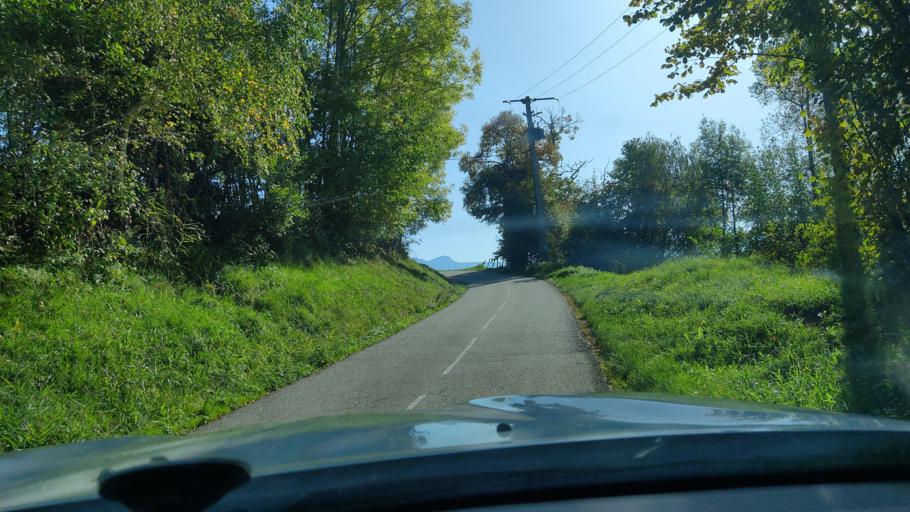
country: FR
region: Rhone-Alpes
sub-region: Departement de la Savoie
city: Les Echelles
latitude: 45.4630
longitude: 5.7594
